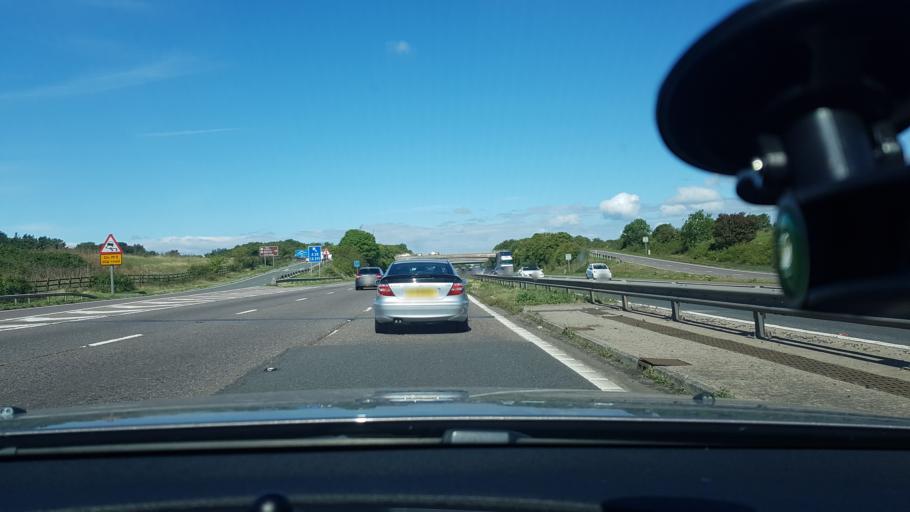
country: GB
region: England
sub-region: Somerset
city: Puriton
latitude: 51.1641
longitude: -2.9815
